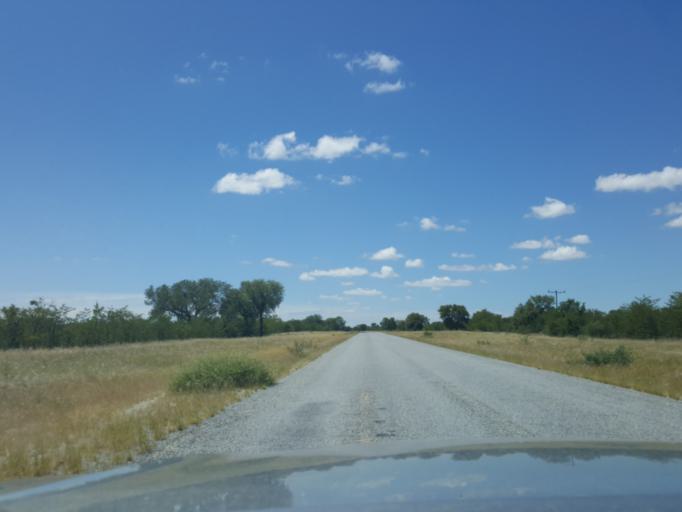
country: BW
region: Central
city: Nata
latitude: -20.1485
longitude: 25.7328
